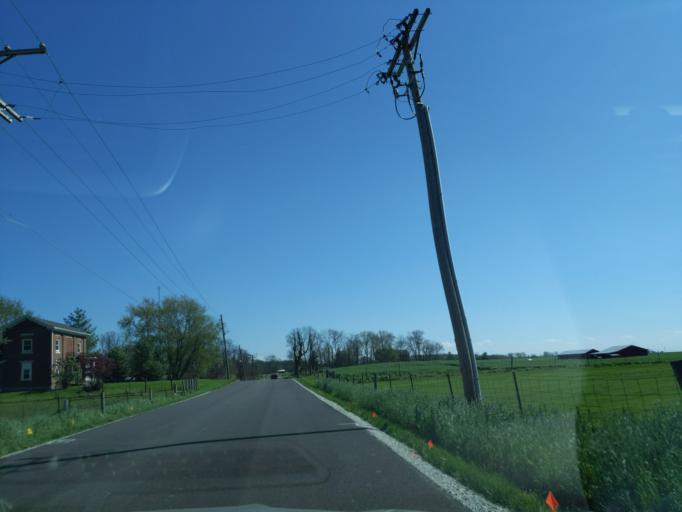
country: US
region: Indiana
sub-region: Decatur County
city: Greensburg
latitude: 39.3205
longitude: -85.4890
